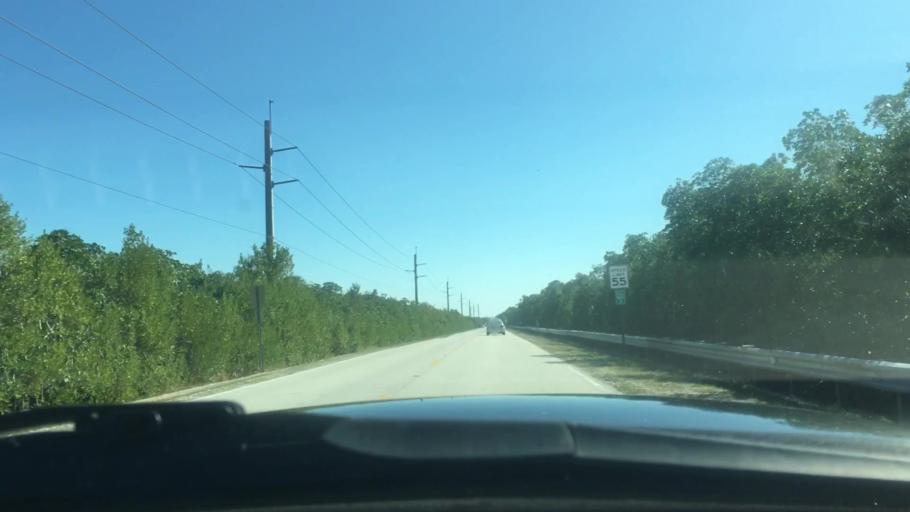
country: US
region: Florida
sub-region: Monroe County
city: North Key Largo
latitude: 25.2812
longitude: -80.3493
